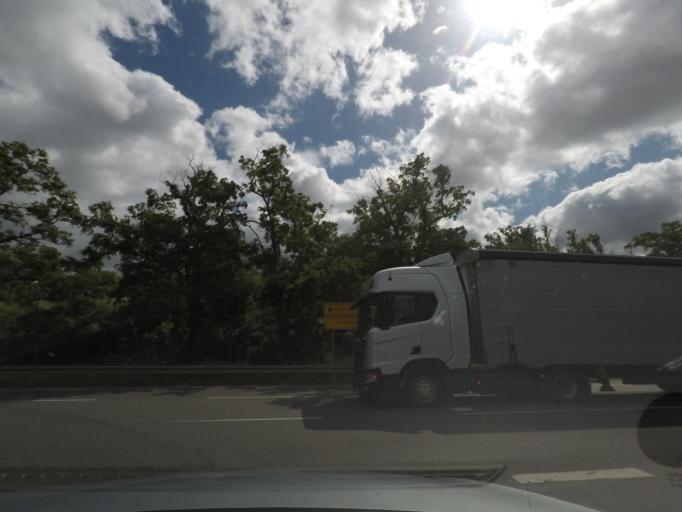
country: DE
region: Saxony-Anhalt
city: Quedlinburg
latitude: 51.8112
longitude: 11.1284
